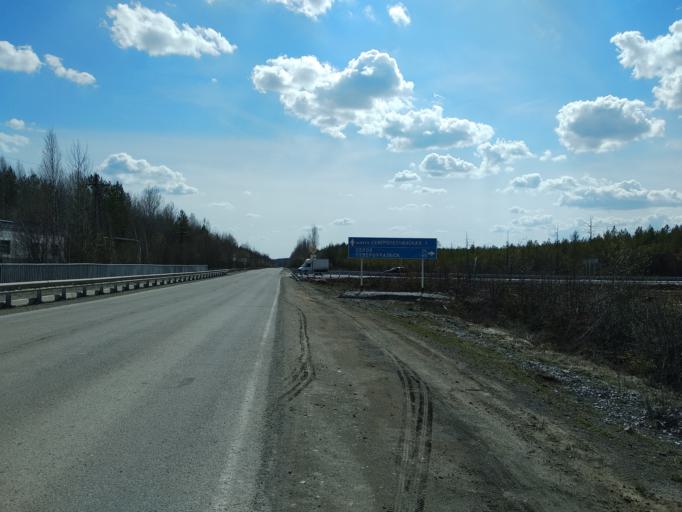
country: RU
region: Sverdlovsk
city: Krasnotur'insk
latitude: 59.7026
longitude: 60.2035
